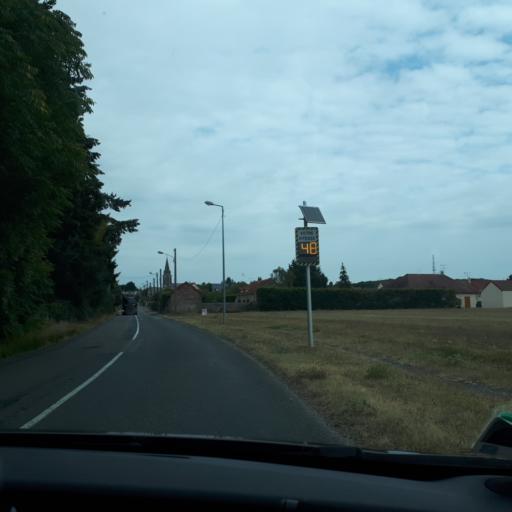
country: FR
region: Centre
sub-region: Departement du Loiret
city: Ouzouer-sur-Loire
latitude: 47.7655
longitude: 2.4745
